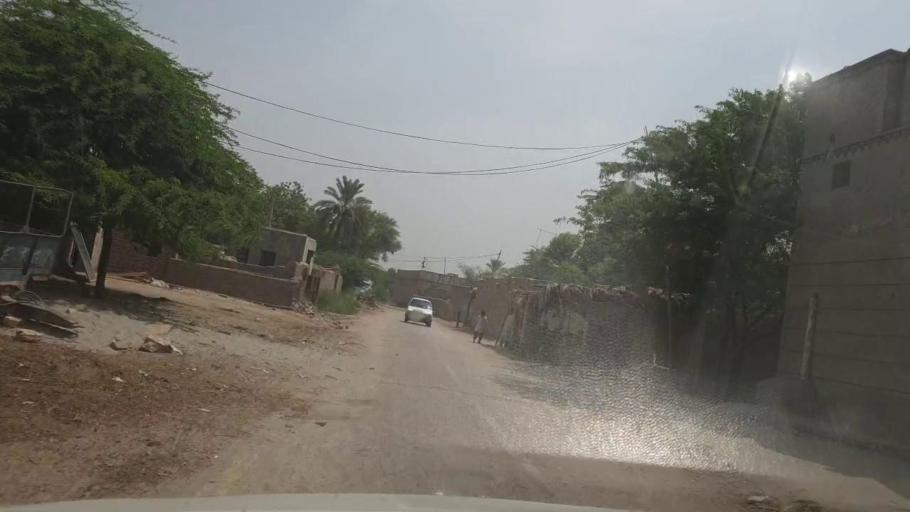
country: PK
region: Sindh
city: Kot Diji
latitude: 27.3719
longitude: 68.6490
